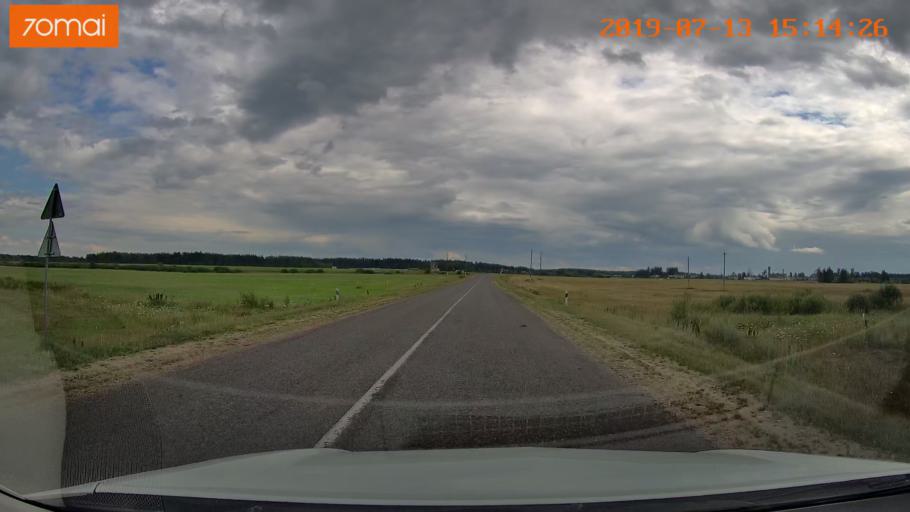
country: BY
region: Mogilev
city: Hlusha
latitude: 53.1274
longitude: 28.8190
